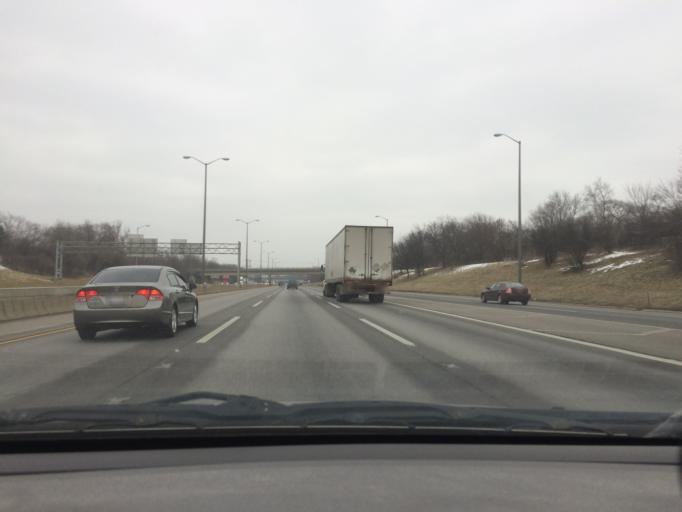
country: US
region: Illinois
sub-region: DuPage County
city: Glendale Heights
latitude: 41.9006
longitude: -88.0381
